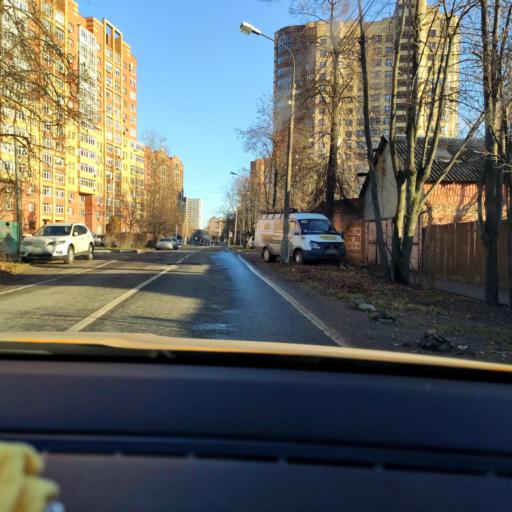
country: RU
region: Moscow
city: Yaroslavskiy
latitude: 55.8957
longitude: 37.7081
